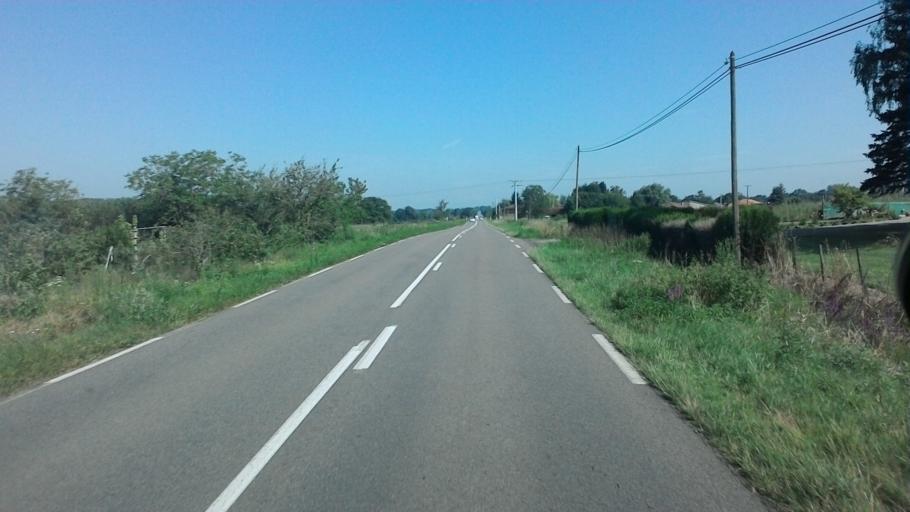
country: FR
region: Rhone-Alpes
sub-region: Departement de l'Ain
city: Saint-Trivier-de-Courtes
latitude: 46.4075
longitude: 5.1068
